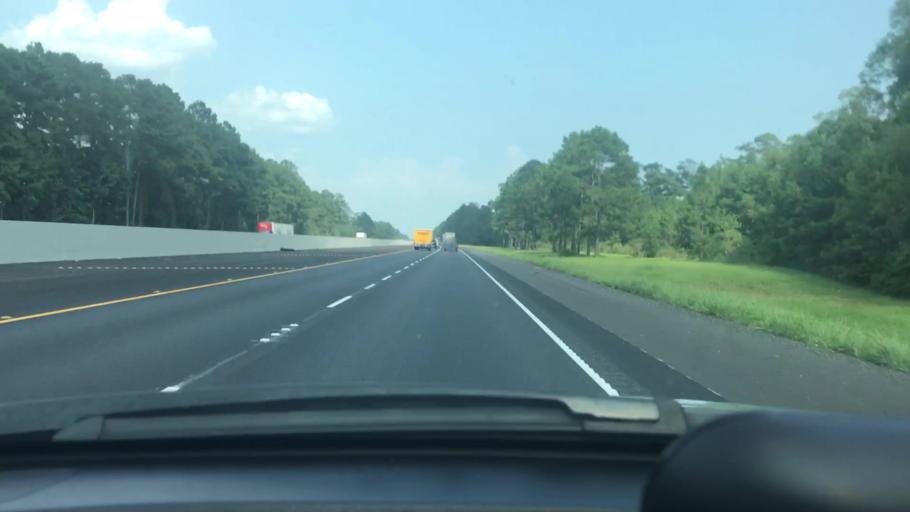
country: US
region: Louisiana
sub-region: Livingston Parish
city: Livingston
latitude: 30.4746
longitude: -90.6693
